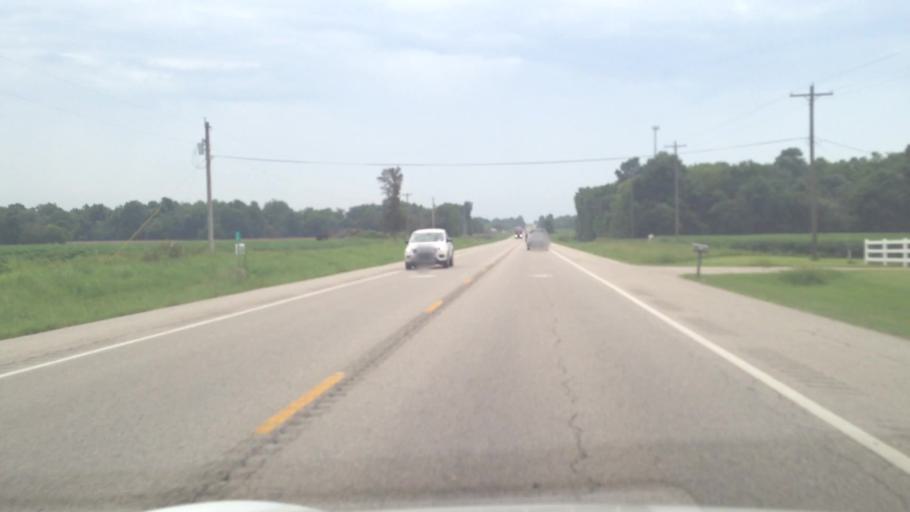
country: US
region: Kansas
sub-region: Cherokee County
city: Galena
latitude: 37.1880
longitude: -94.7046
